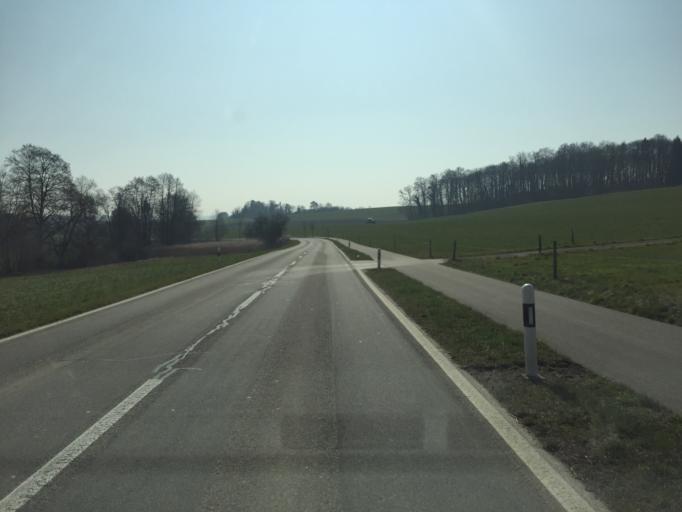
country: CH
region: Thurgau
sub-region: Frauenfeld District
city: Huttwilen
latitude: 47.6022
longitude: 8.8776
